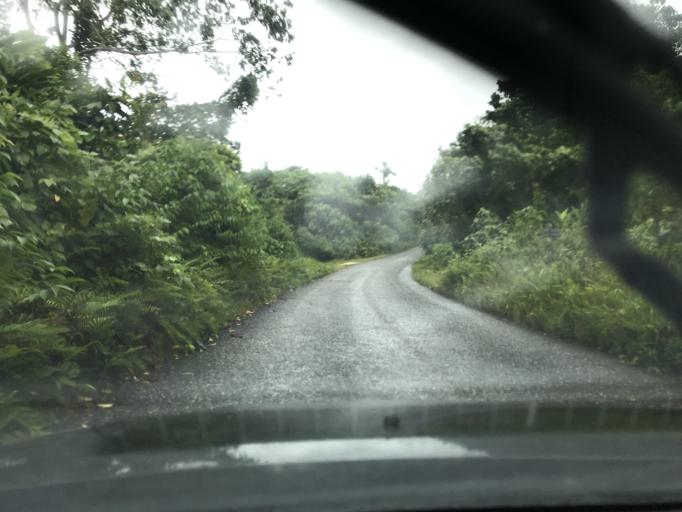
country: SB
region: Western Province
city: Gizo
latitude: -8.2657
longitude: 157.2355
